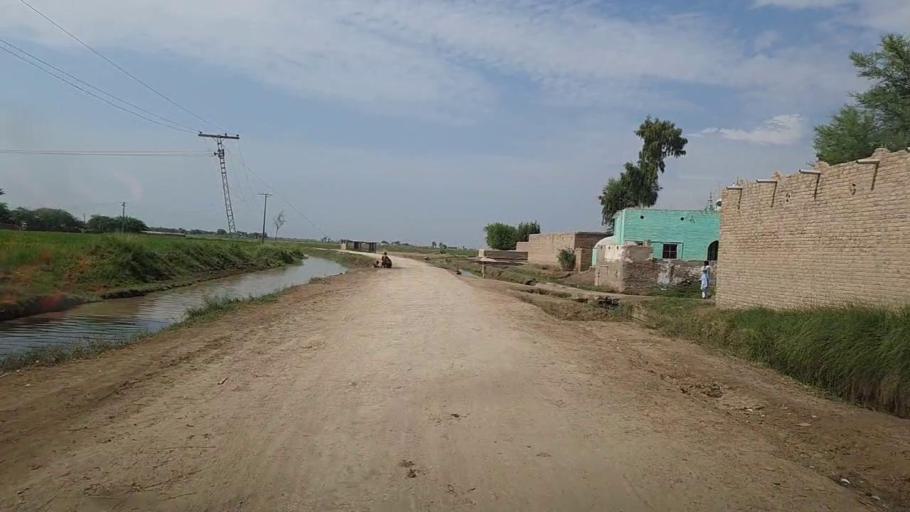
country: PK
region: Sindh
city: Thul
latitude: 28.2543
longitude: 68.8069
